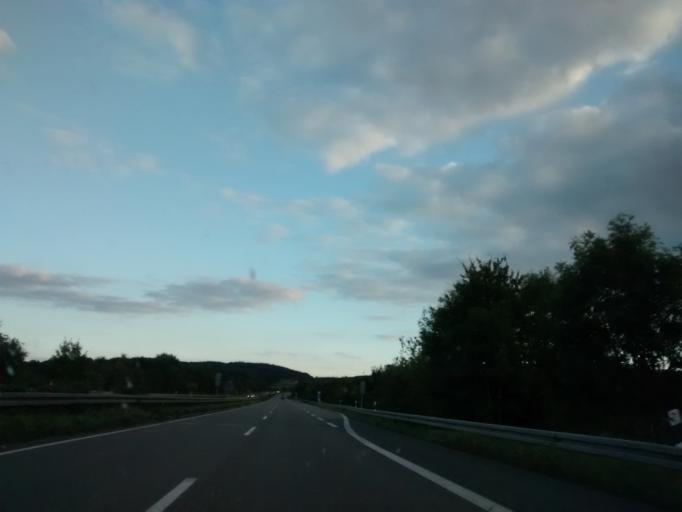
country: DE
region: Lower Saxony
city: Hilter
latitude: 52.1734
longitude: 8.1539
